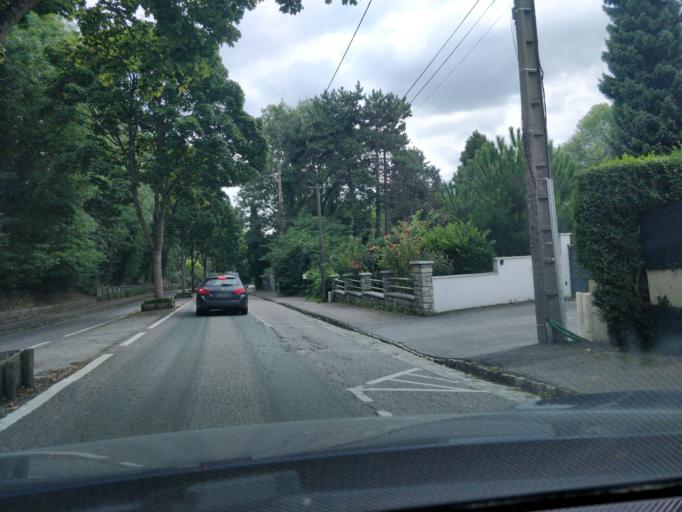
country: FR
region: Haute-Normandie
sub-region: Departement de la Seine-Maritime
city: Mont-Saint-Aignan
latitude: 49.4677
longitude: 1.1047
